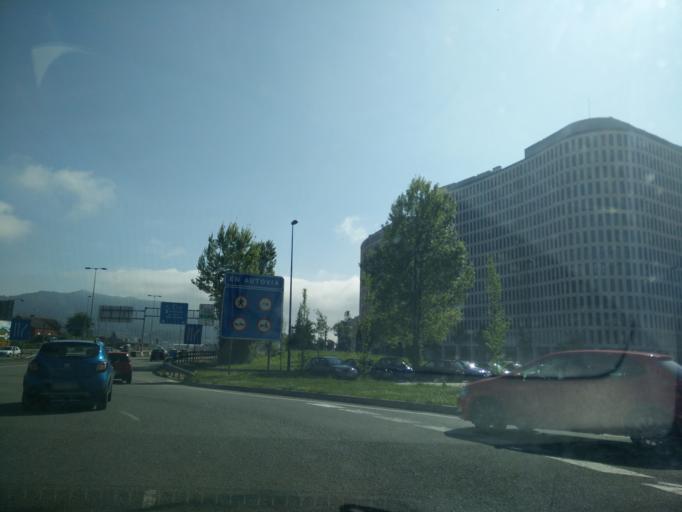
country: ES
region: Galicia
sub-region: Provincia de Pontevedra
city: Vigo
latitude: 42.2109
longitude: -8.7528
